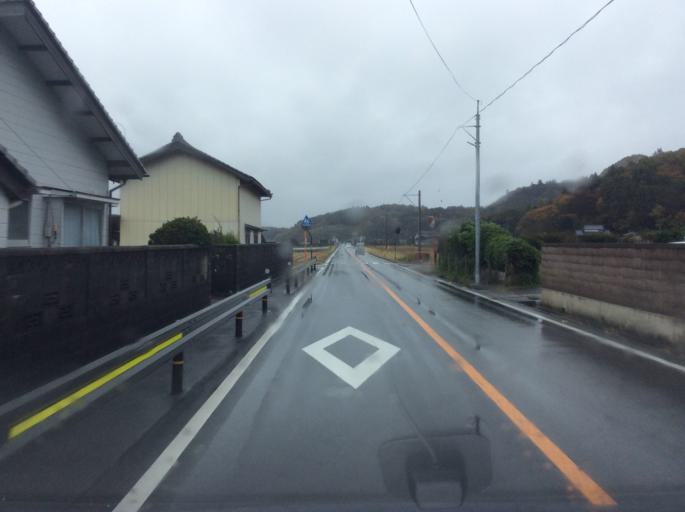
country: JP
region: Fukushima
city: Iwaki
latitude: 37.1048
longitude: 140.9536
